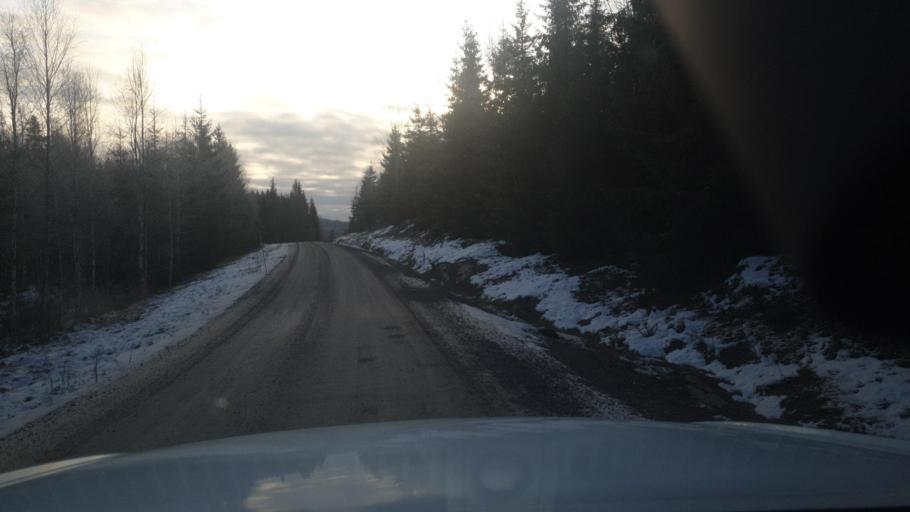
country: SE
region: Vaermland
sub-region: Arvika Kommun
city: Arvika
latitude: 59.9473
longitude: 12.6614
